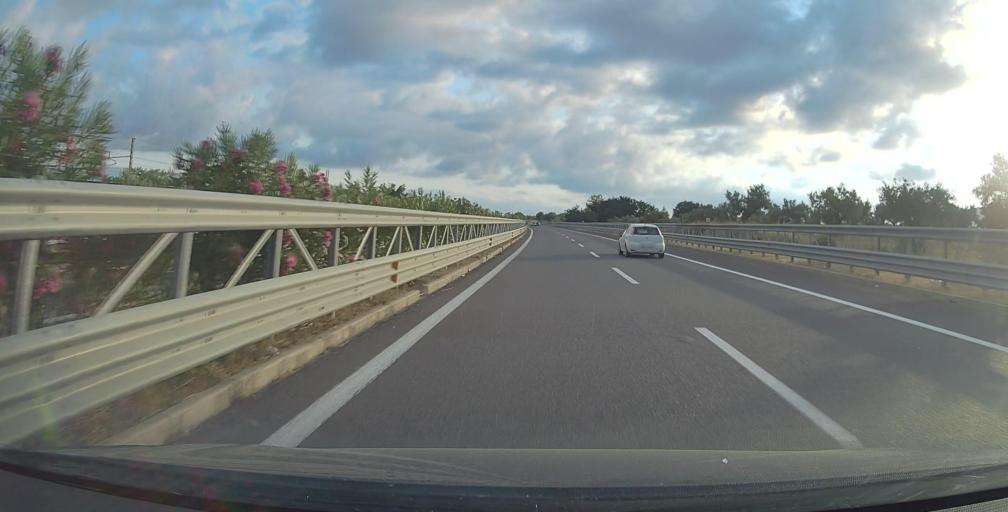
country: IT
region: Calabria
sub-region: Provincia di Catanzaro
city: Acconia
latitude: 38.8273
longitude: 16.2523
